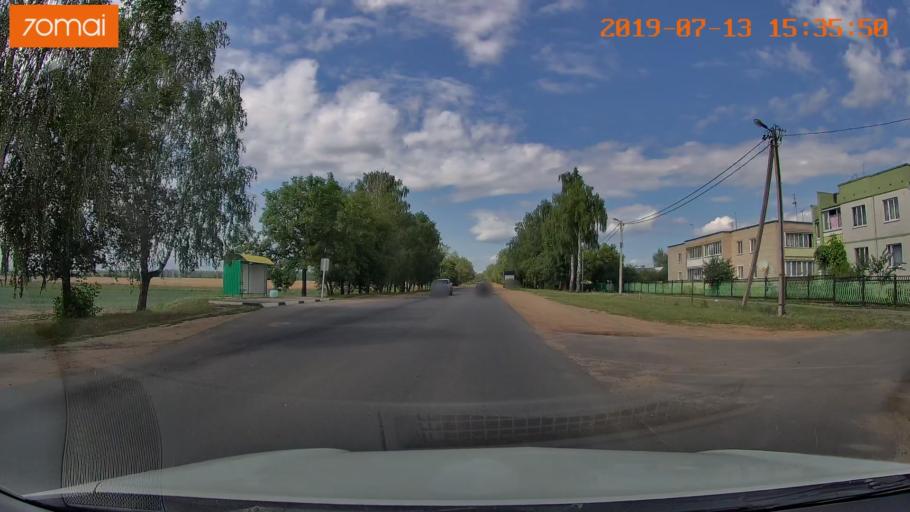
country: BY
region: Mogilev
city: Babruysk
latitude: 53.1262
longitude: 29.1667
